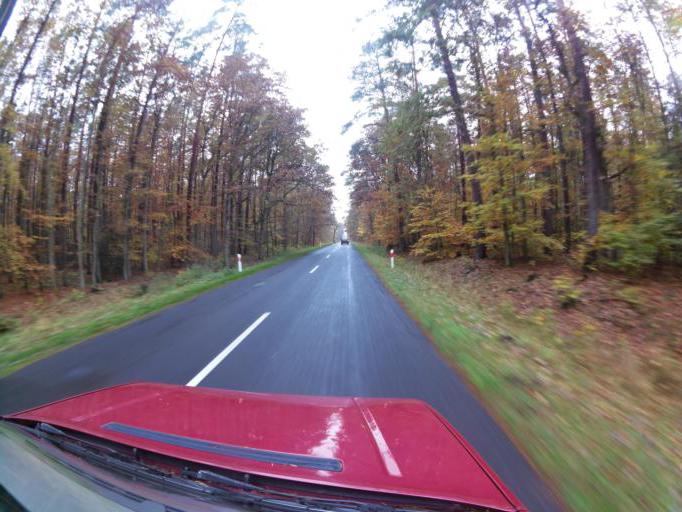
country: PL
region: West Pomeranian Voivodeship
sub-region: Powiat policki
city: Dobra
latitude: 53.5583
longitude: 14.4504
